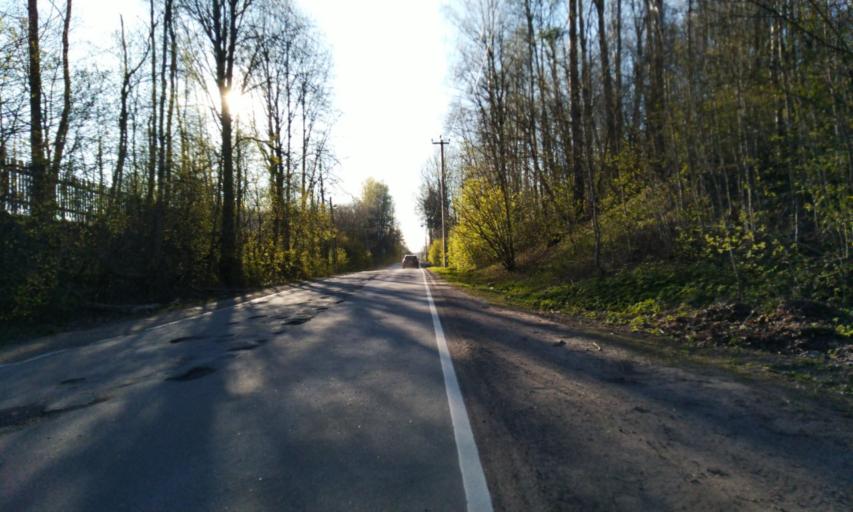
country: RU
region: Leningrad
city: Toksovo
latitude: 60.1406
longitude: 30.5398
